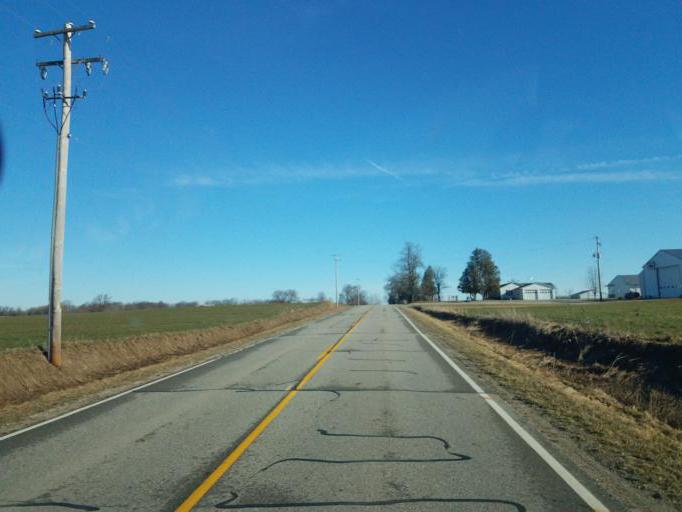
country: US
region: Michigan
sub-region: Montcalm County
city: Edmore
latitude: 43.4788
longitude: -85.0850
